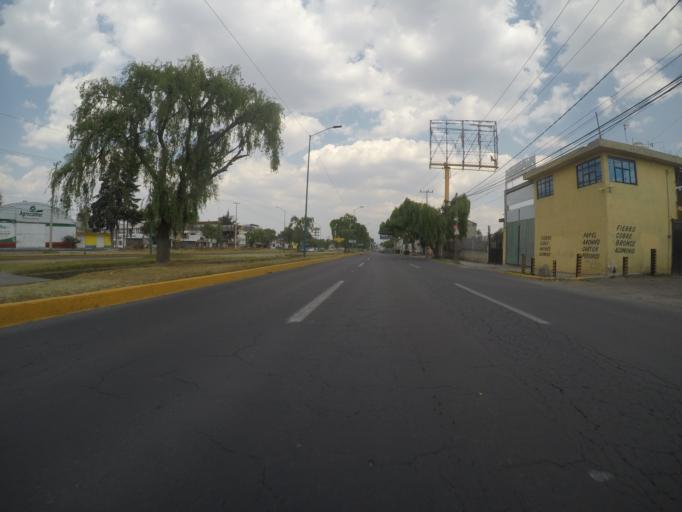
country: MX
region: Mexico
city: San Buenaventura
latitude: 19.2564
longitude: -99.6659
